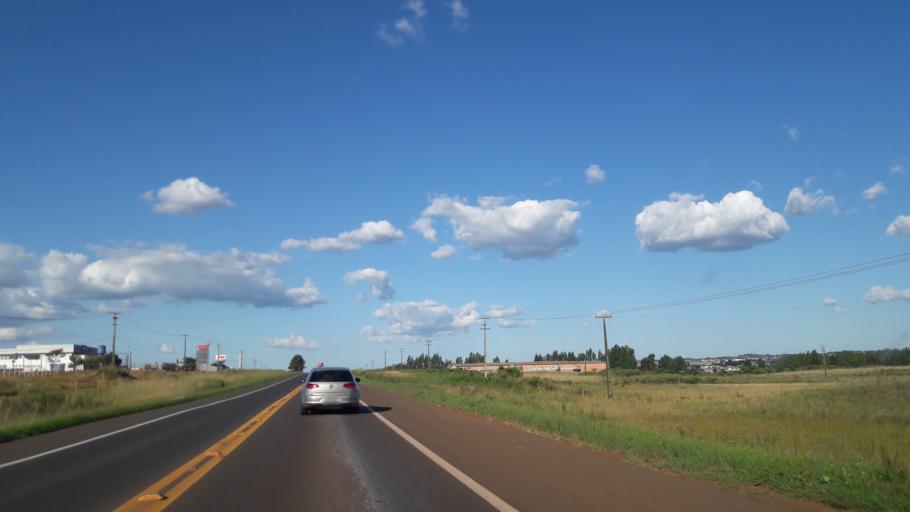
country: BR
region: Parana
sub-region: Guarapuava
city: Guarapuava
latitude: -25.3838
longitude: -51.5125
